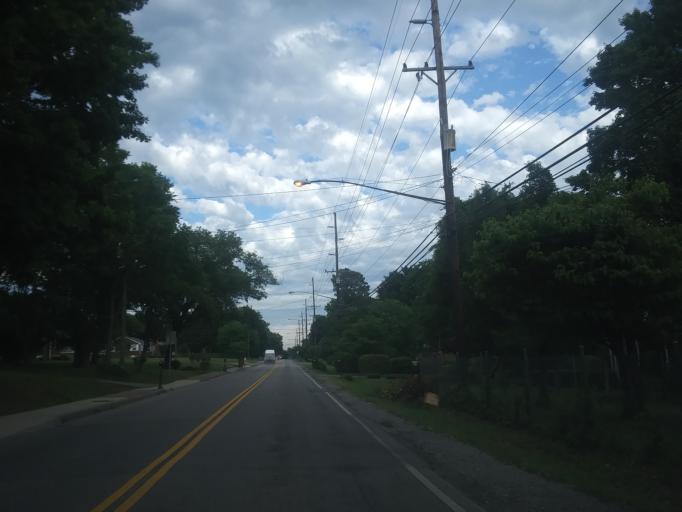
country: US
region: Tennessee
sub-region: Davidson County
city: Oak Hill
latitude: 36.0986
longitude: -86.7297
